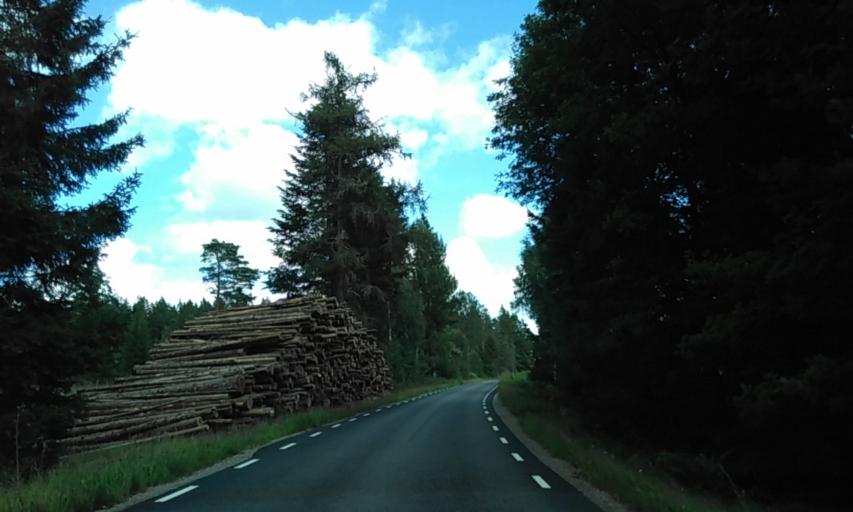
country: SE
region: Vaestra Goetaland
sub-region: Vargarda Kommun
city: Vargarda
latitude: 57.9681
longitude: 12.8807
